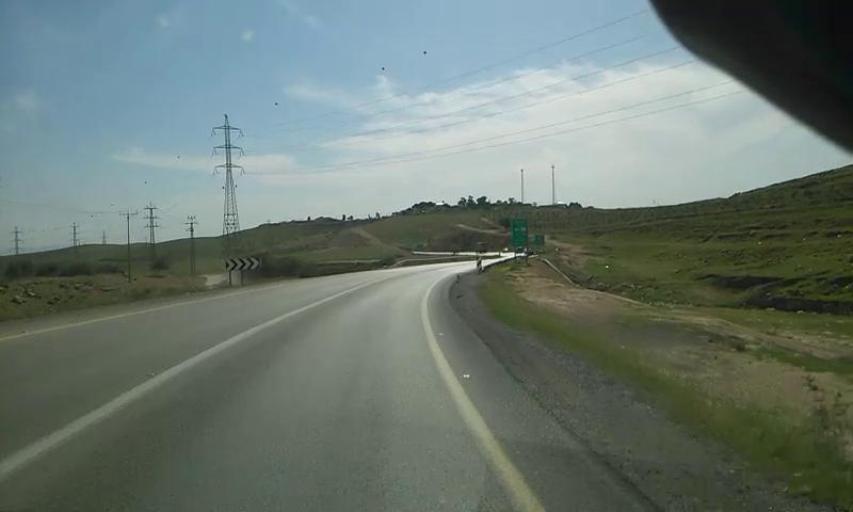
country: PS
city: Az Za`ayyim
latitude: 31.8084
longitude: 35.3217
